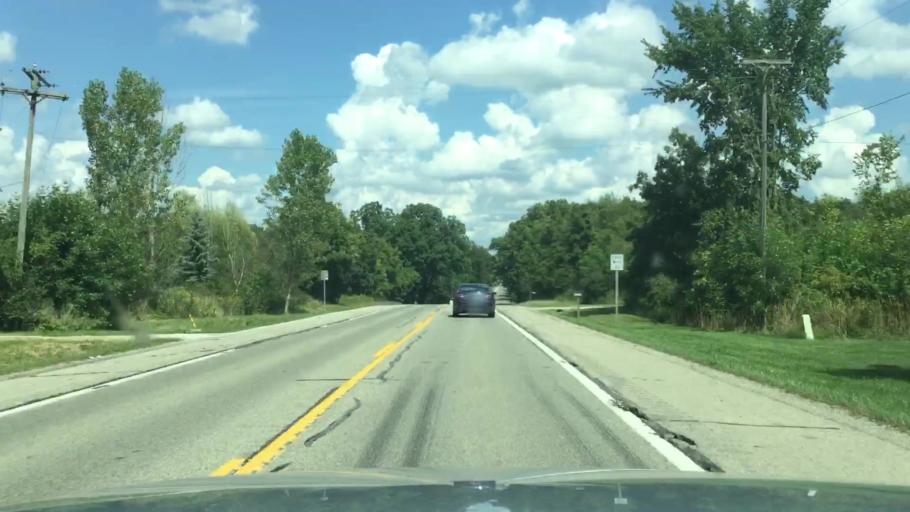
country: US
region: Michigan
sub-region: Lenawee County
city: Clinton
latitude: 42.1114
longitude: -83.8871
